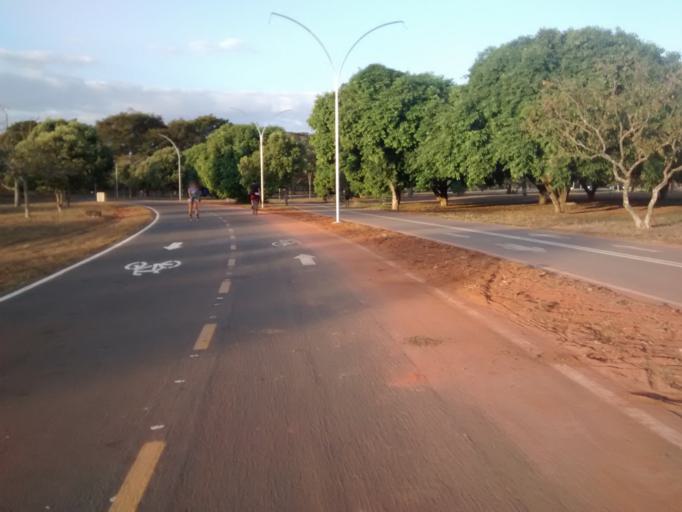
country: BR
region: Federal District
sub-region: Brasilia
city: Brasilia
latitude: -15.8041
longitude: -47.9114
